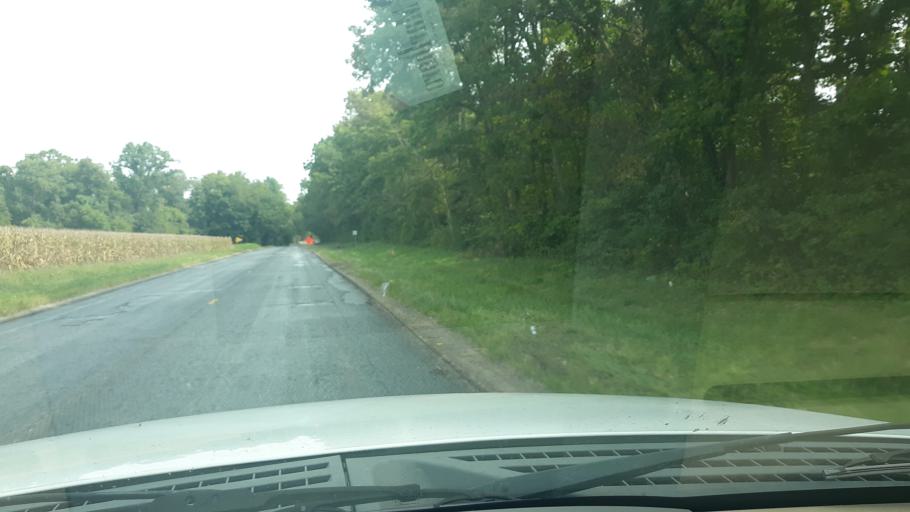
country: US
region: Illinois
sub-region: Edwards County
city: Grayville
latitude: 38.2828
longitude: -87.9820
